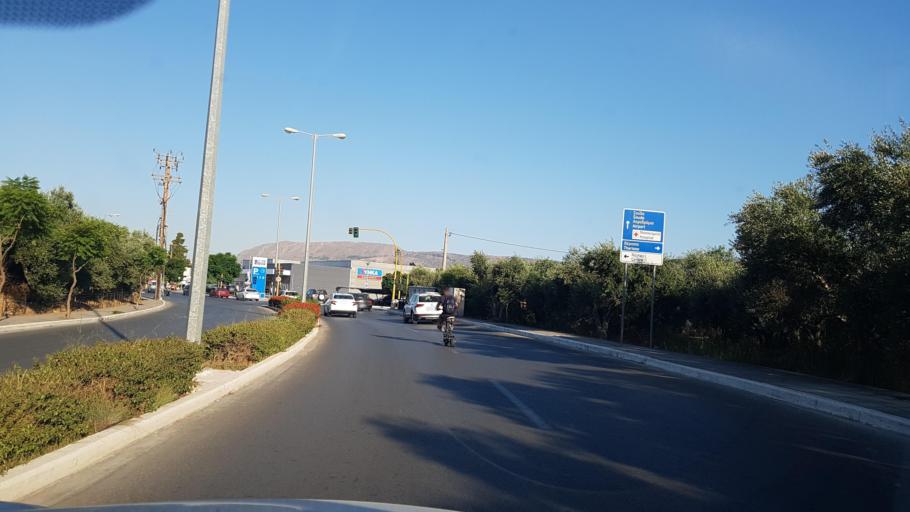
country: GR
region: Crete
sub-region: Nomos Chanias
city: Perivolia
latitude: 35.5046
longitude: 24.0057
